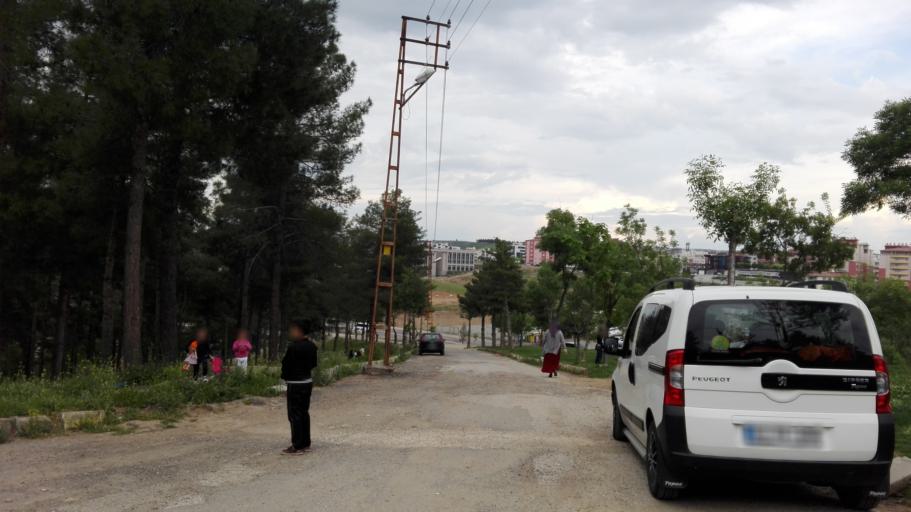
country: TR
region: Batman
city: Demiryol
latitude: 37.9081
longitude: 41.1315
